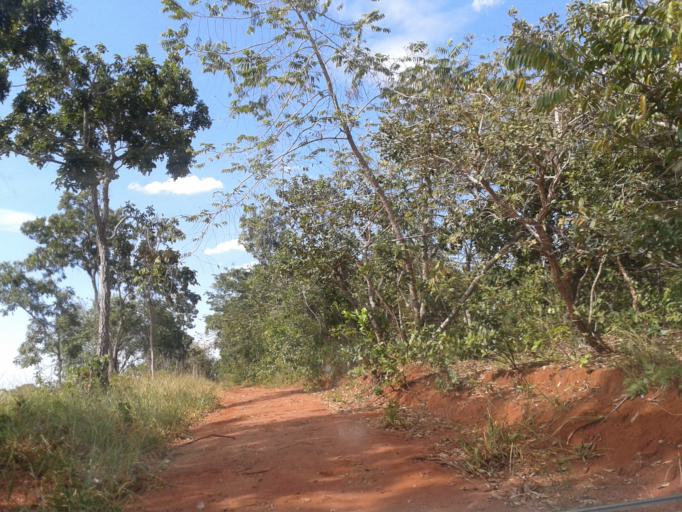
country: BR
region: Minas Gerais
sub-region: Campina Verde
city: Campina Verde
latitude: -19.3957
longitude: -49.7352
